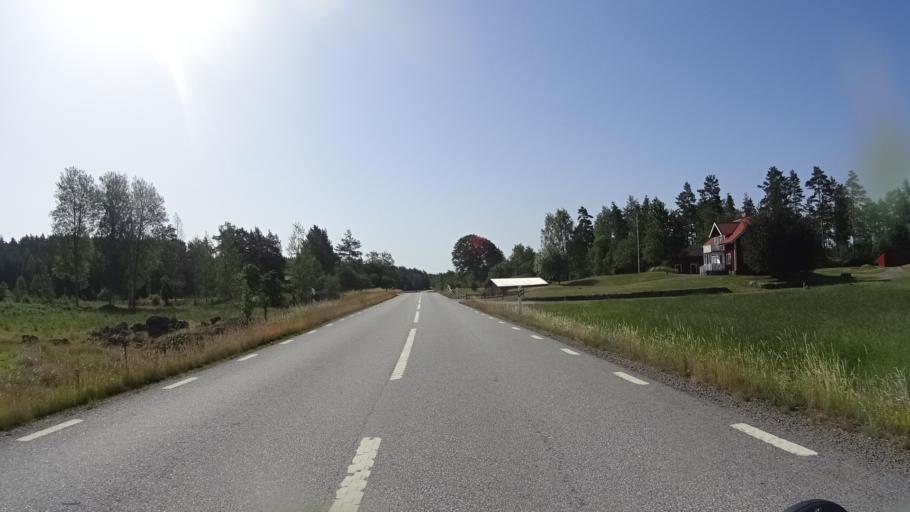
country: SE
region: OEstergoetland
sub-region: Atvidabergs Kommun
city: Atvidaberg
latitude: 58.0861
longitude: 16.1433
